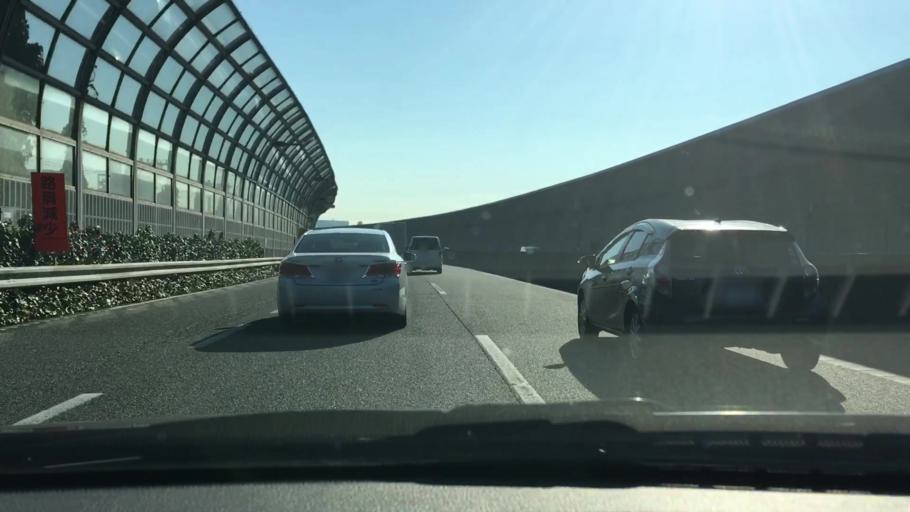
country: JP
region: Chiba
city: Funabashi
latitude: 35.6951
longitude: 139.9757
